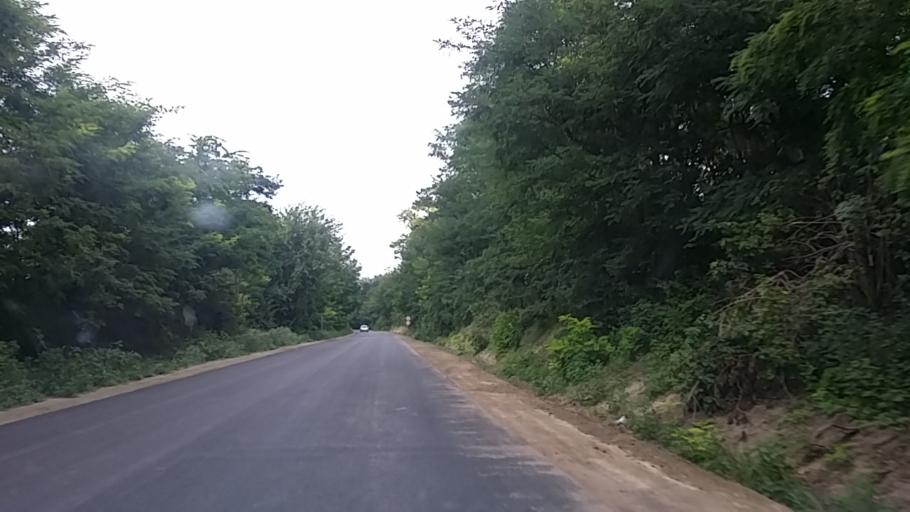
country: HU
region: Tolna
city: Tengelic
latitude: 46.5511
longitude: 18.7180
